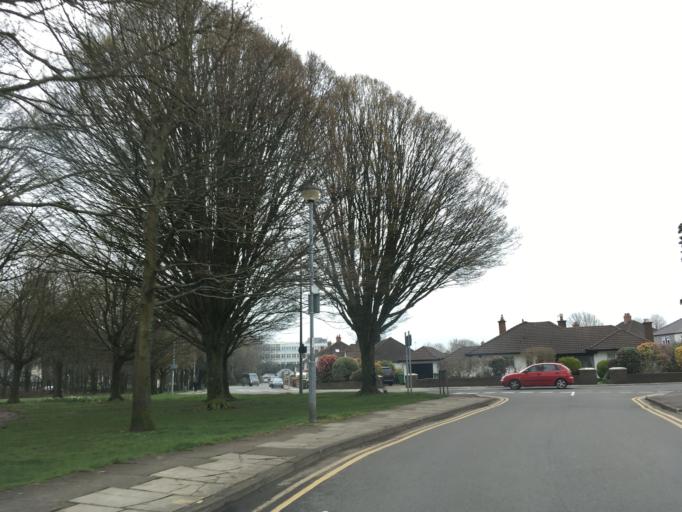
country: GB
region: Wales
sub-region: Cardiff
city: Cardiff
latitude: 51.5098
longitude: -3.1922
